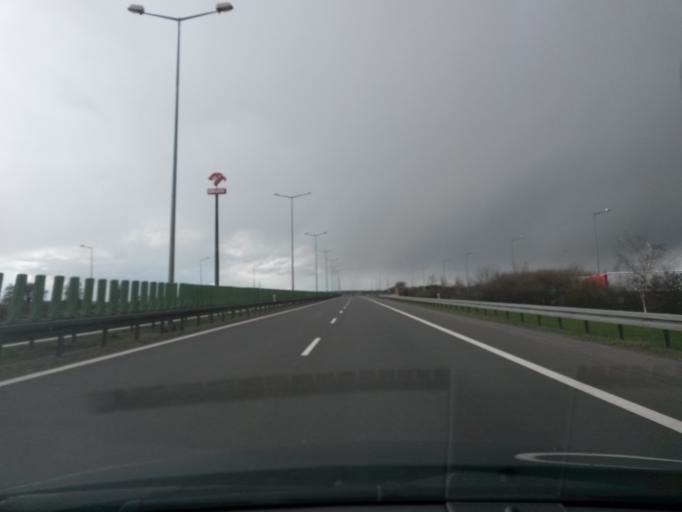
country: PL
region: Greater Poland Voivodeship
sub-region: Powiat poznanski
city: Kleszczewo
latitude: 52.3287
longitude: 17.0923
